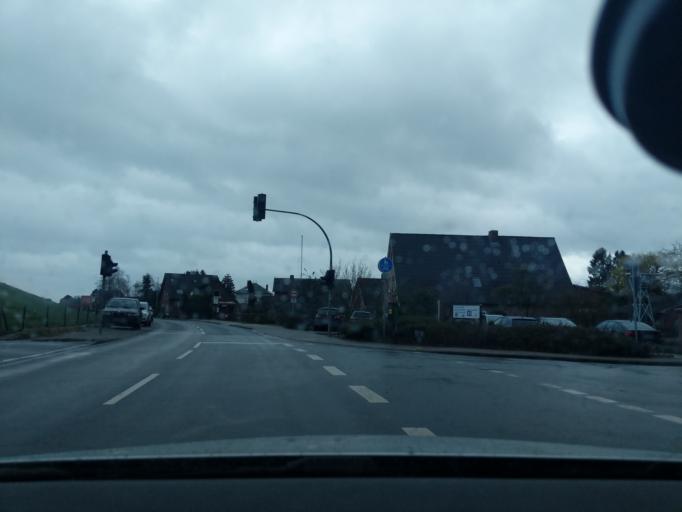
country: DE
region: Lower Saxony
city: Grunendeich
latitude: 53.5761
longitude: 9.6128
